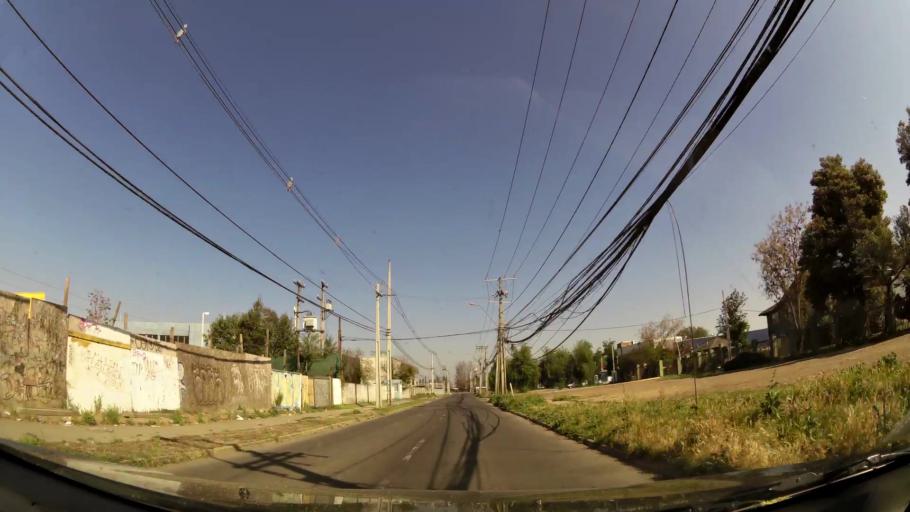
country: CL
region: Santiago Metropolitan
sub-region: Provincia de Chacabuco
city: Chicureo Abajo
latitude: -33.3621
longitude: -70.6794
